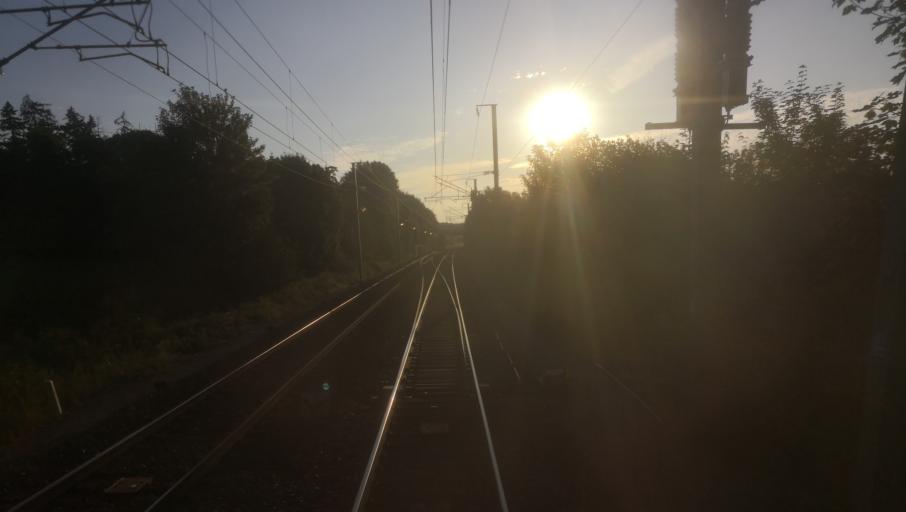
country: FR
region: Lower Normandy
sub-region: Departement du Calvados
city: La Vespiere
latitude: 49.0772
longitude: 0.3854
